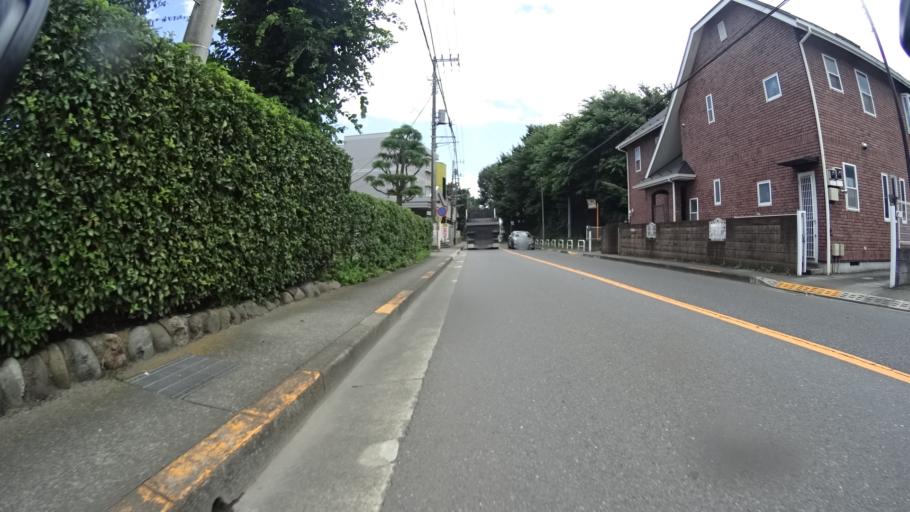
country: JP
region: Tokyo
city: Fussa
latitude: 35.7316
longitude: 139.3305
